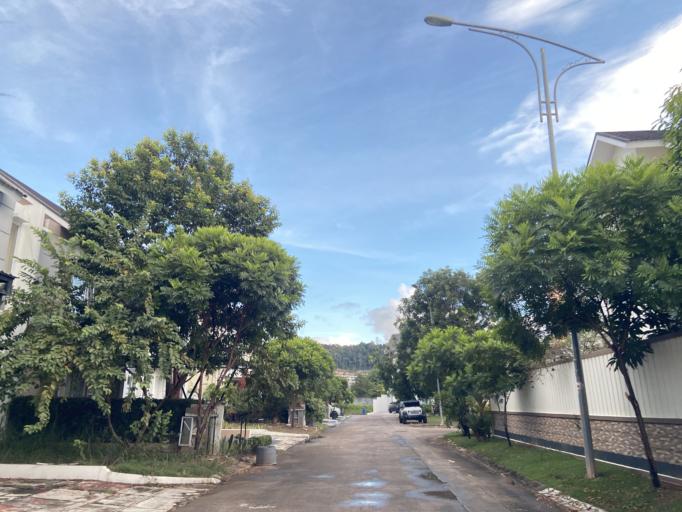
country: SG
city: Singapore
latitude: 1.0904
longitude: 104.0331
